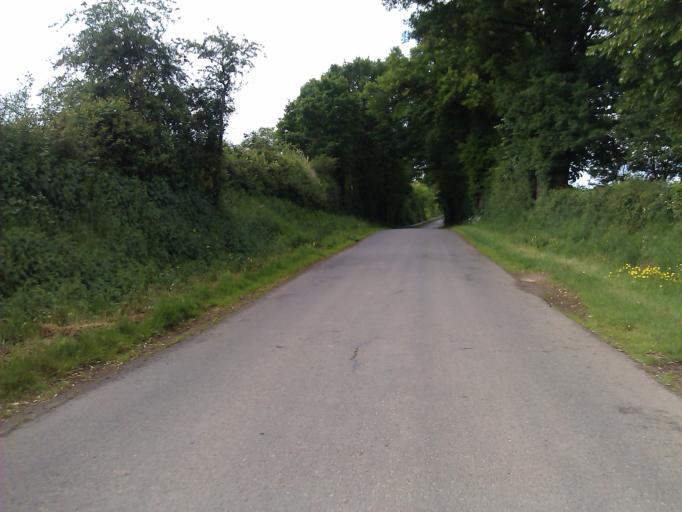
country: FR
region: Poitou-Charentes
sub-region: Departement de la Vienne
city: Availles-Limouzine
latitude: 46.1237
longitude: 0.5848
